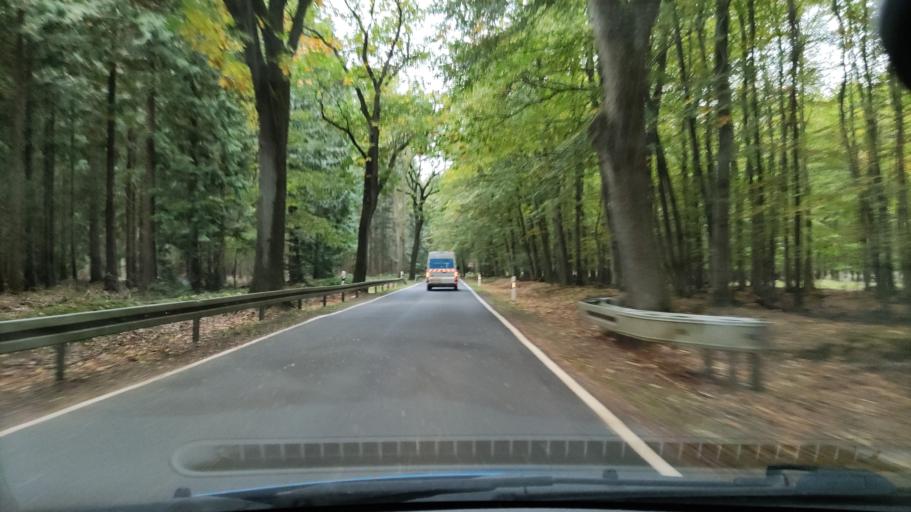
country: DE
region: Mecklenburg-Vorpommern
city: Zarrentin
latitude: 53.4537
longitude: 10.9404
